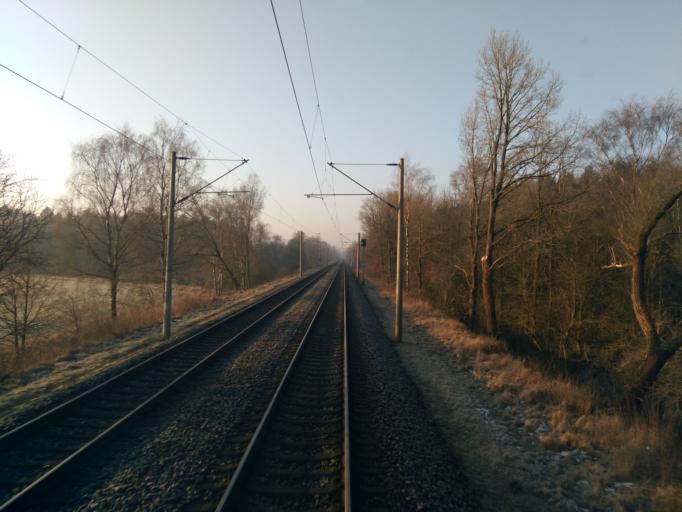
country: DE
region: Lower Saxony
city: Buchholz in der Nordheide
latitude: 53.3423
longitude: 9.9048
